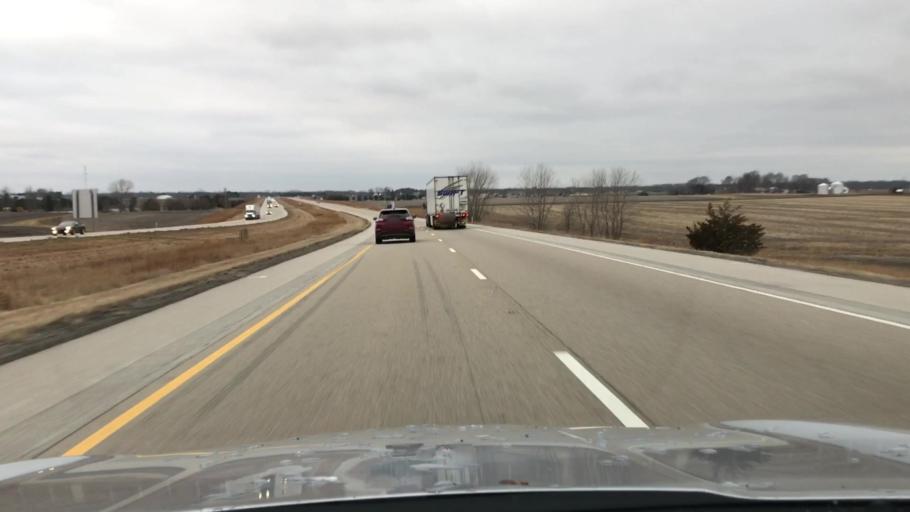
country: US
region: Illinois
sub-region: Logan County
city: Lincoln
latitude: 40.1852
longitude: -89.3244
